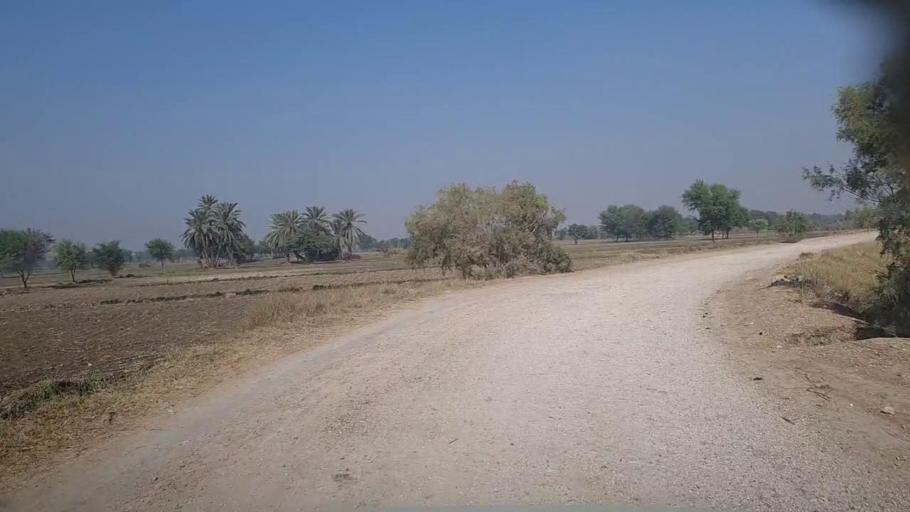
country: PK
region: Sindh
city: Kandiari
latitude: 26.9306
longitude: 68.5237
